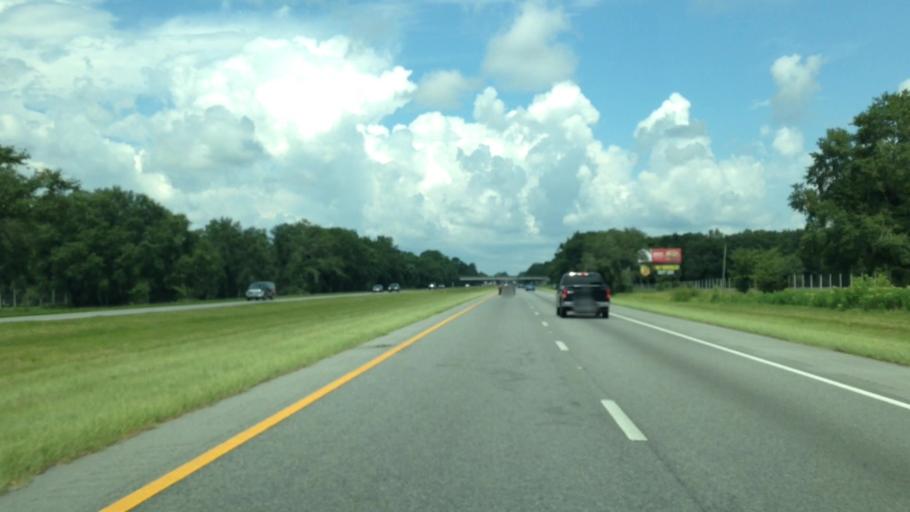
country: US
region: Florida
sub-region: Madison County
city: Madison
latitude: 30.4011
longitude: -83.3814
